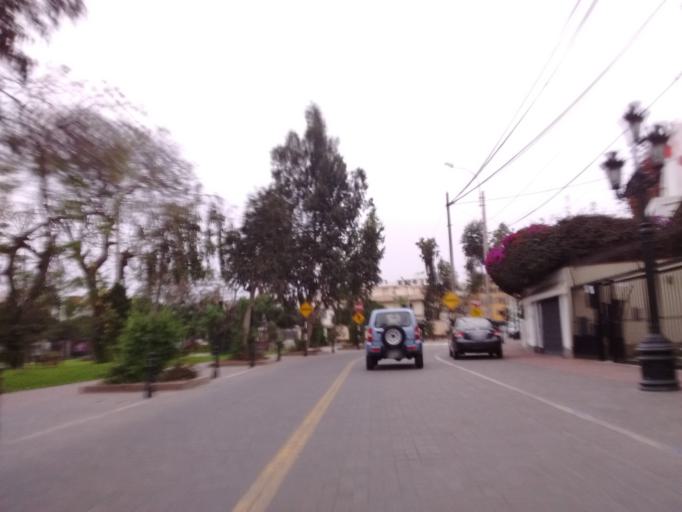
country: PE
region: Lima
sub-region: Lima
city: San Isidro
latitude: -12.0731
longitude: -77.0712
